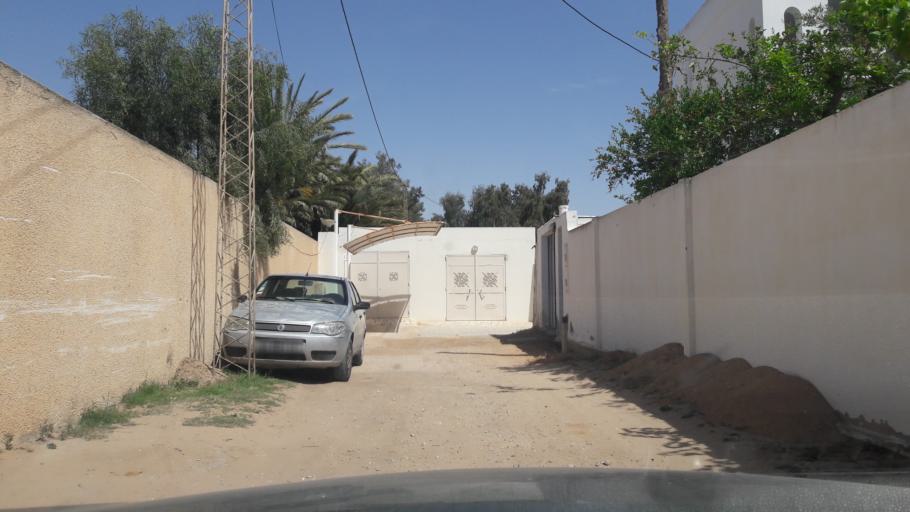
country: TN
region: Safaqis
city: Al Qarmadah
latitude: 34.7896
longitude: 10.7586
